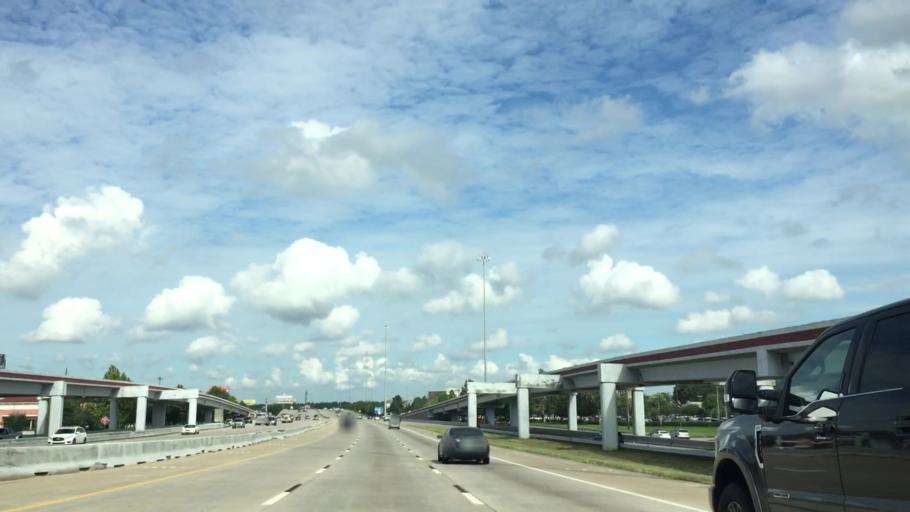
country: US
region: Texas
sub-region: Harris County
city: Jersey Village
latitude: 29.9627
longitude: -95.5497
